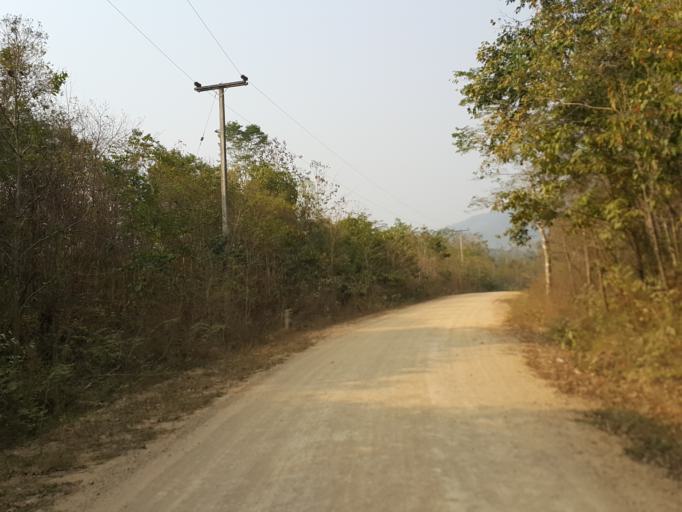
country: TH
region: Lampang
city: Mae Phrik
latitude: 17.5959
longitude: 98.9732
